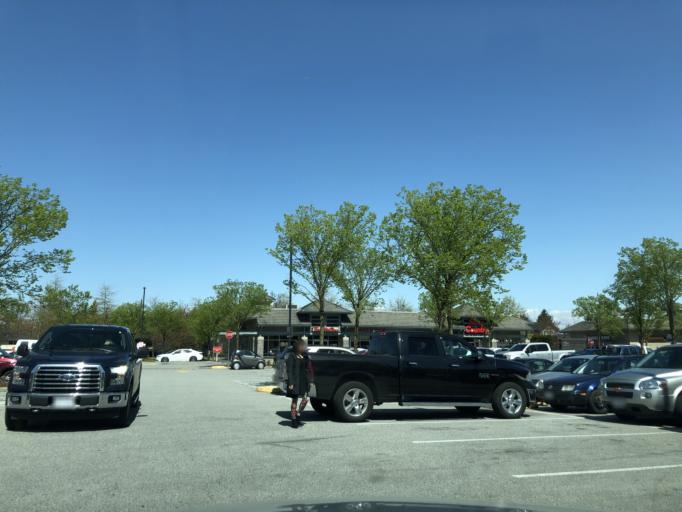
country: CA
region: British Columbia
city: Ladner
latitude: 49.1324
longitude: -123.0985
